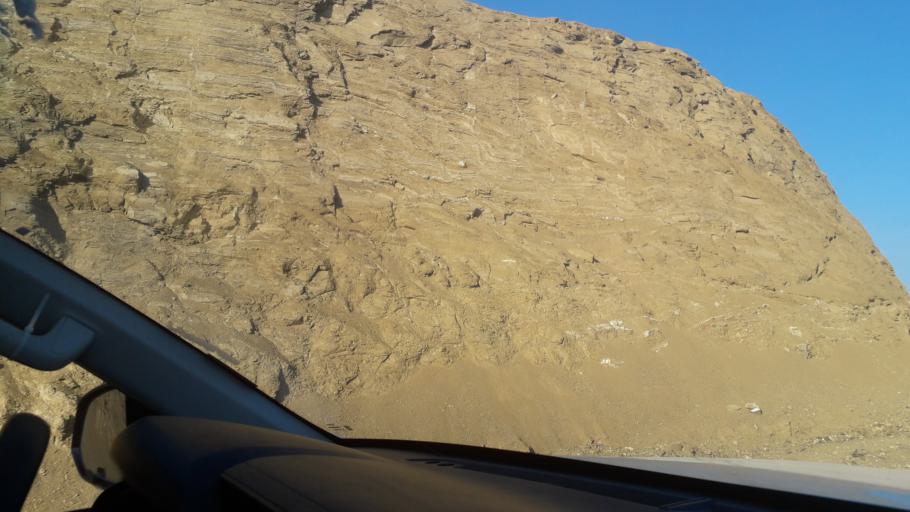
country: ET
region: Amhara
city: Dese
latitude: 11.5176
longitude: 39.2512
